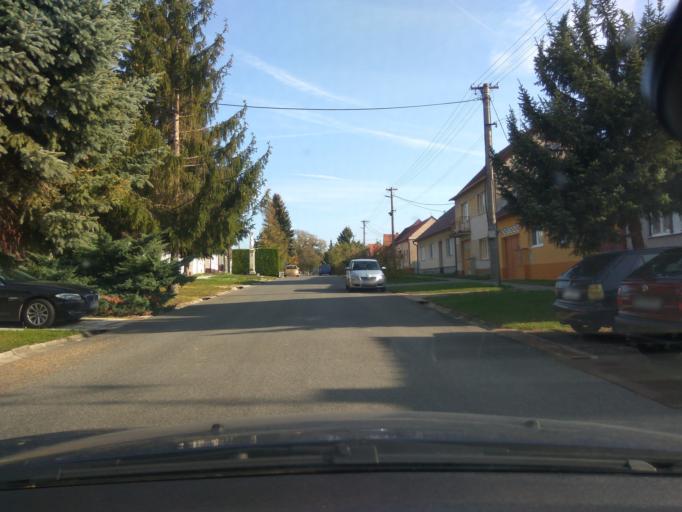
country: SK
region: Trnavsky
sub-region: Okres Senica
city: Senica
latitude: 48.6236
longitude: 17.4380
